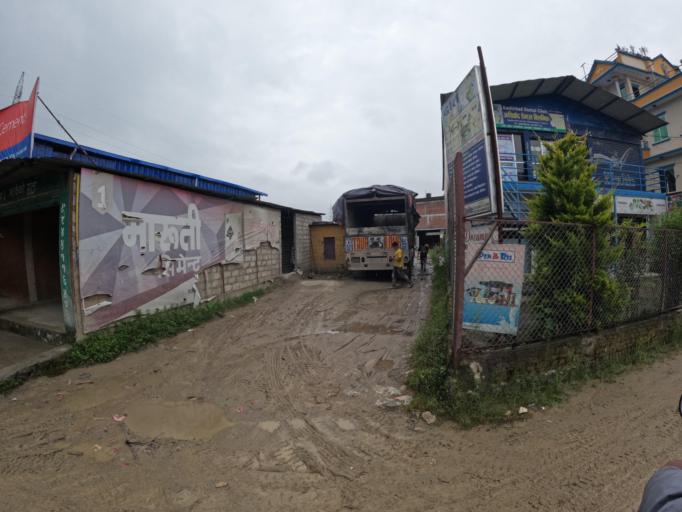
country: NP
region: Central Region
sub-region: Bagmati Zone
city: Kathmandu
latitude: 27.7623
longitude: 85.3189
